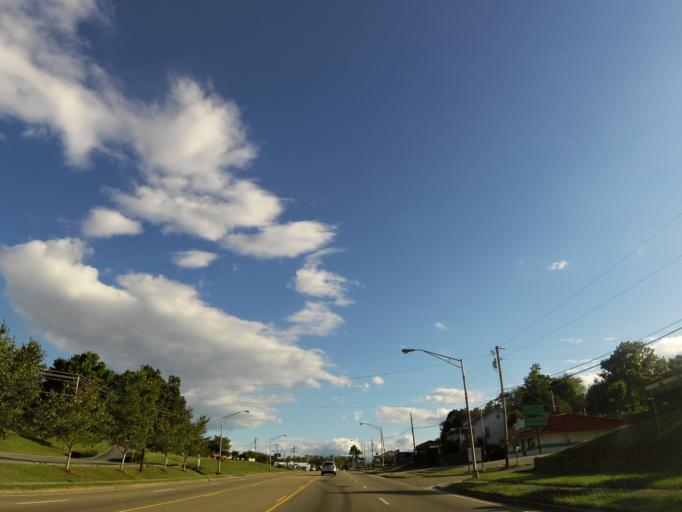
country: US
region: Tennessee
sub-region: Cocke County
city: Newport
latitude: 35.9600
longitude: -83.1954
